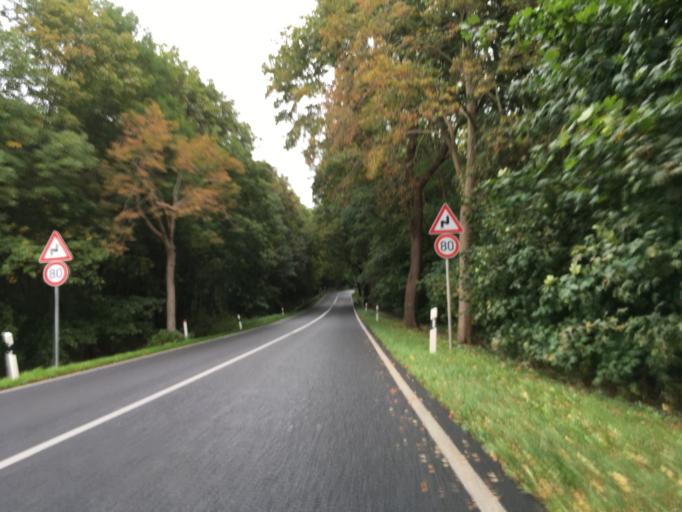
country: DE
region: Brandenburg
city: Werftpfuhl
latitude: 52.6869
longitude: 13.8522
